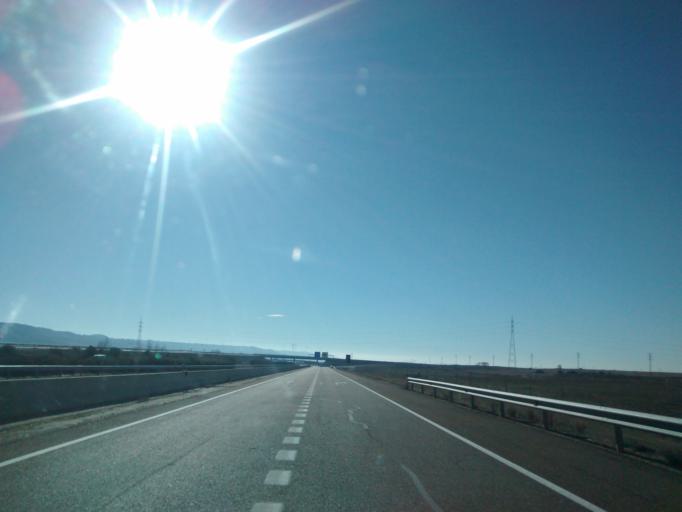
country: ES
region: Castille and Leon
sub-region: Provincia de Palencia
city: Fuentes de Valdepero
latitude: 42.0663
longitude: -4.4929
